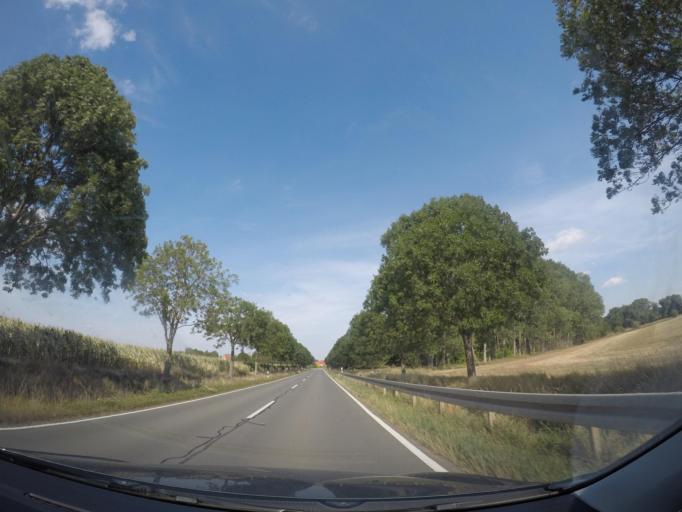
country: DE
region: Saxony-Anhalt
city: Langeln
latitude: 51.9419
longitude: 10.8183
